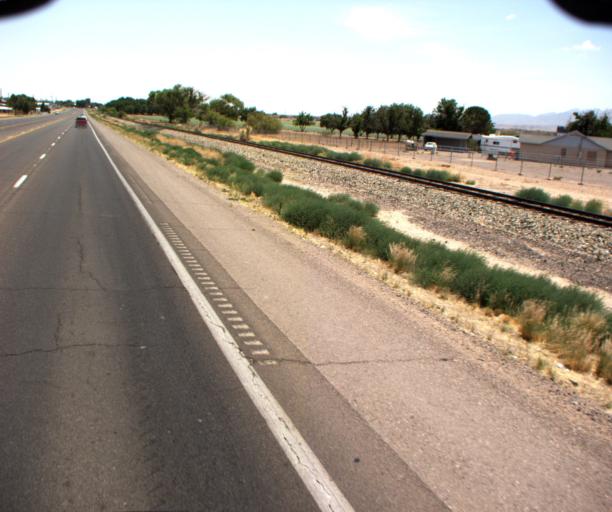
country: US
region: Arizona
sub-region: Graham County
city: Thatcher
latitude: 32.8587
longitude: -109.7839
